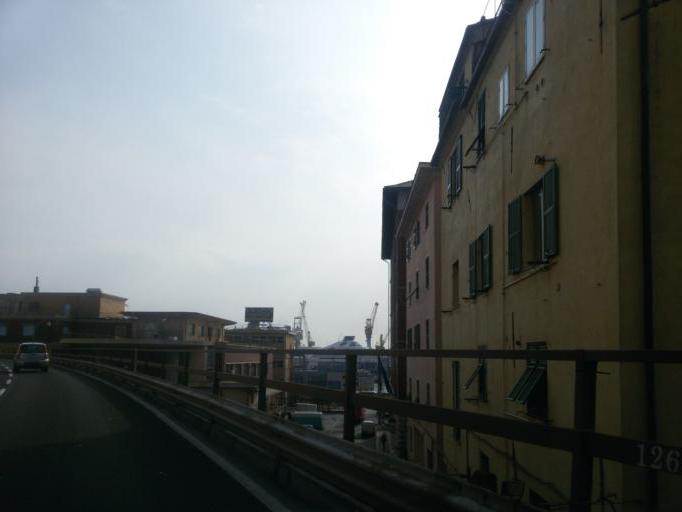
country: IT
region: Liguria
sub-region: Provincia di Genova
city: San Teodoro
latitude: 44.4066
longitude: 8.9275
